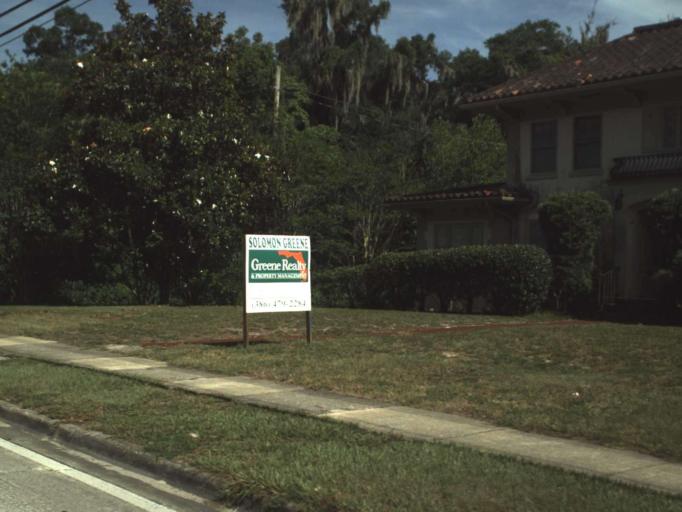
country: US
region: Florida
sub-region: Volusia County
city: DeLand
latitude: 29.0281
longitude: -81.2943
